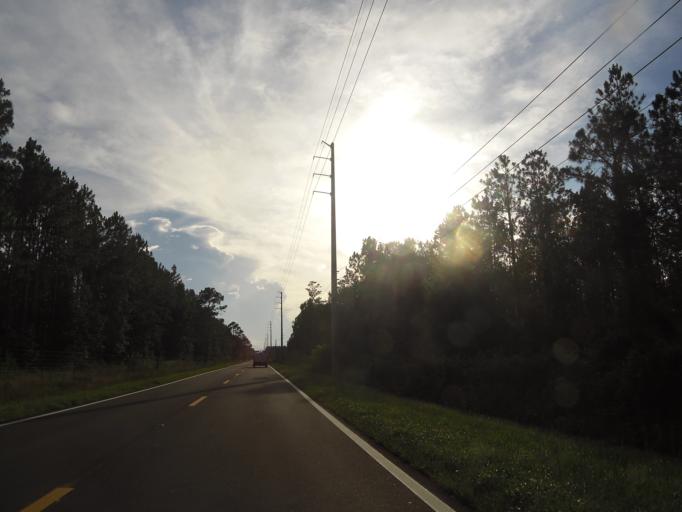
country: US
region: Florida
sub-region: Clay County
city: Green Cove Springs
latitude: 30.0148
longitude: -81.5770
